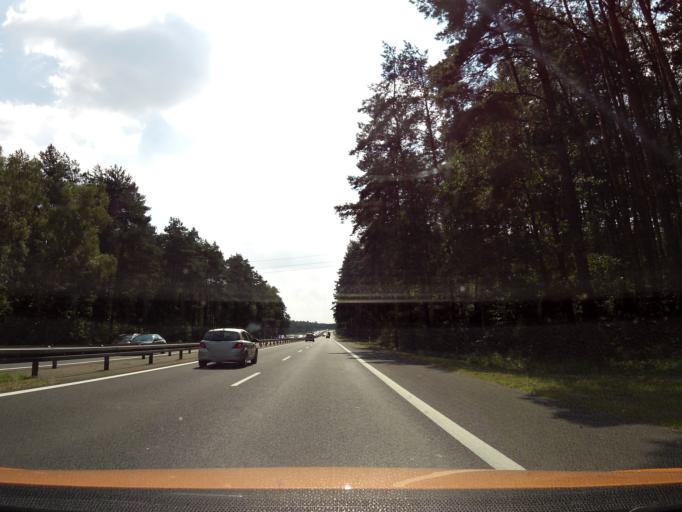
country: PL
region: West Pomeranian Voivodeship
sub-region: Powiat goleniowski
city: Goleniow
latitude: 53.5397
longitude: 14.8060
